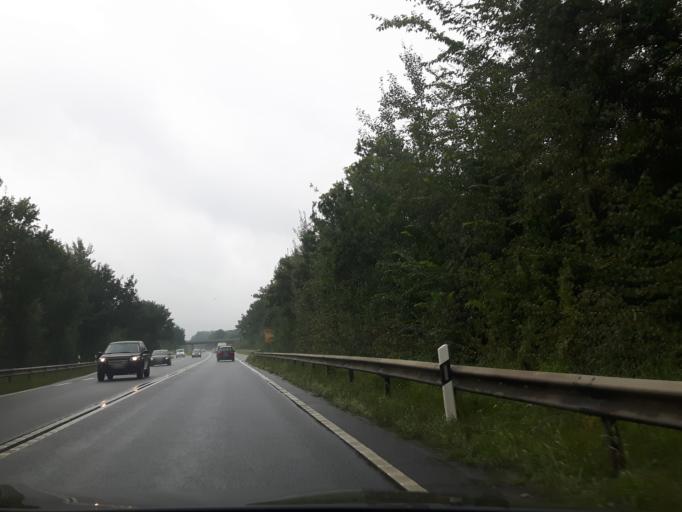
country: DE
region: Lower Saxony
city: Lingen
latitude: 52.5208
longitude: 7.3512
